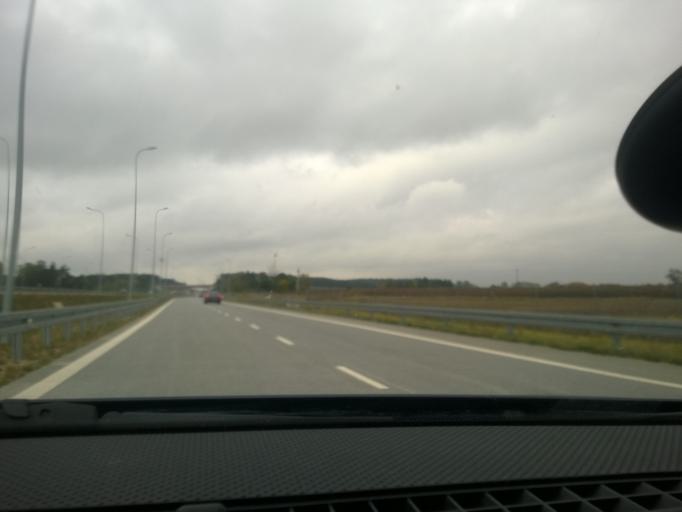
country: PL
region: Lodz Voivodeship
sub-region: Powiat lodzki wschodni
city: Tuszyn
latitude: 51.6421
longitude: 19.5733
